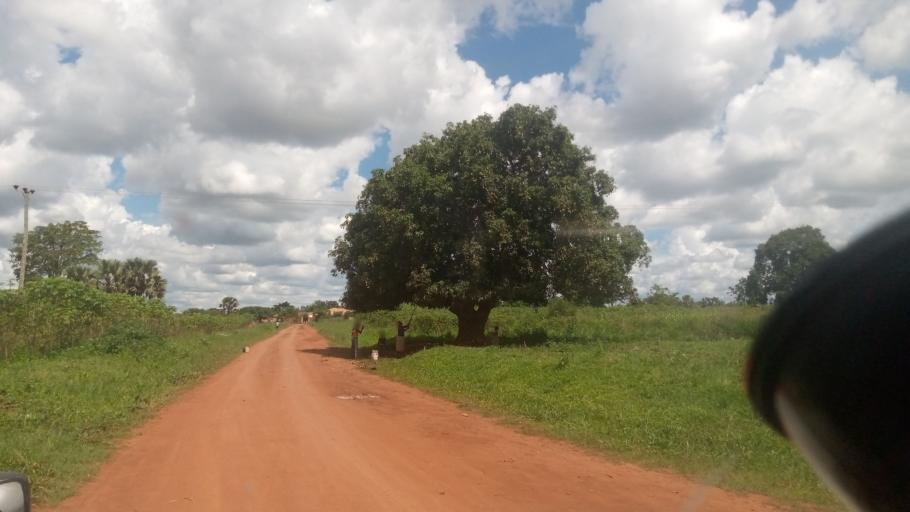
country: UG
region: Northern Region
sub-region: Lira District
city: Lira
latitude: 2.2356
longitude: 32.9072
